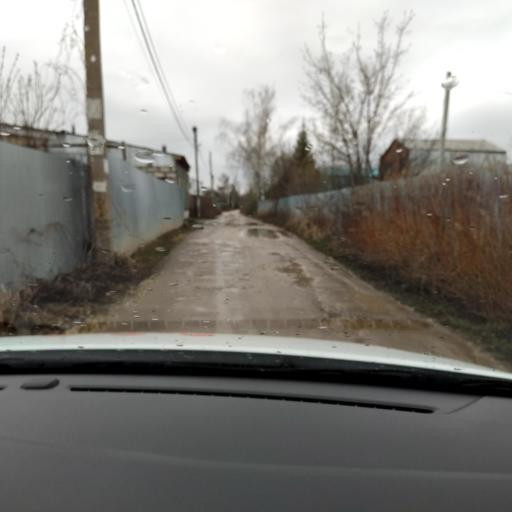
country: RU
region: Tatarstan
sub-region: Gorod Kazan'
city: Kazan
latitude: 55.6894
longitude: 49.0710
